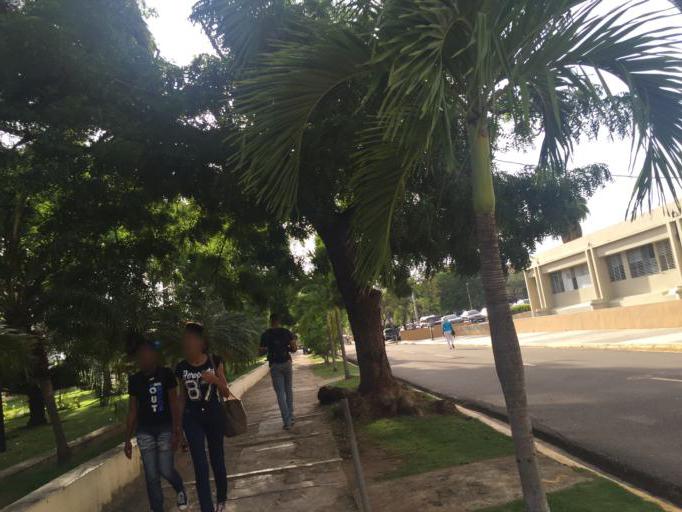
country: DO
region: Nacional
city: La Julia
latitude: 18.4618
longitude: -69.9180
